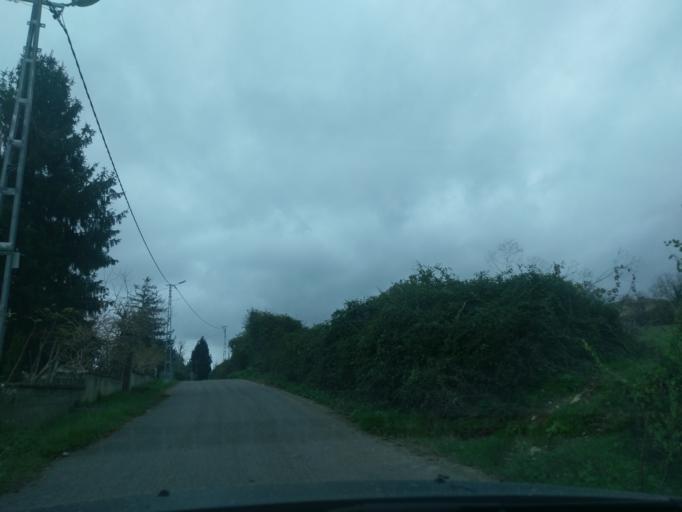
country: TR
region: Istanbul
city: Catalca
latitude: 41.1602
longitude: 28.4431
